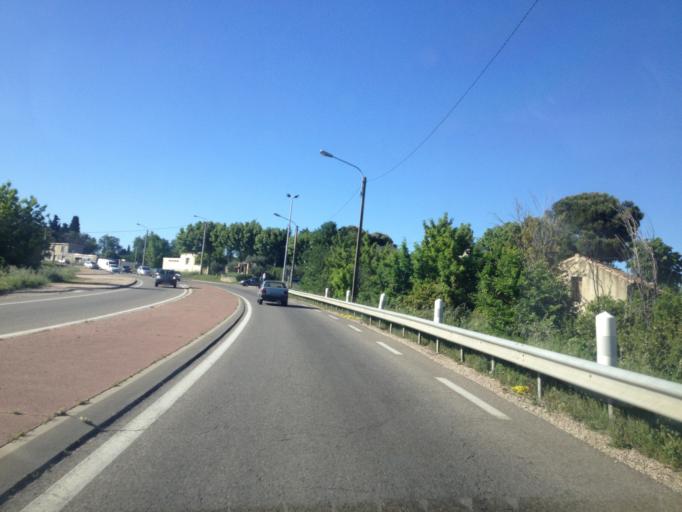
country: FR
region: Provence-Alpes-Cote d'Azur
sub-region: Departement du Vaucluse
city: Courthezon
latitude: 44.0907
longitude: 4.8780
